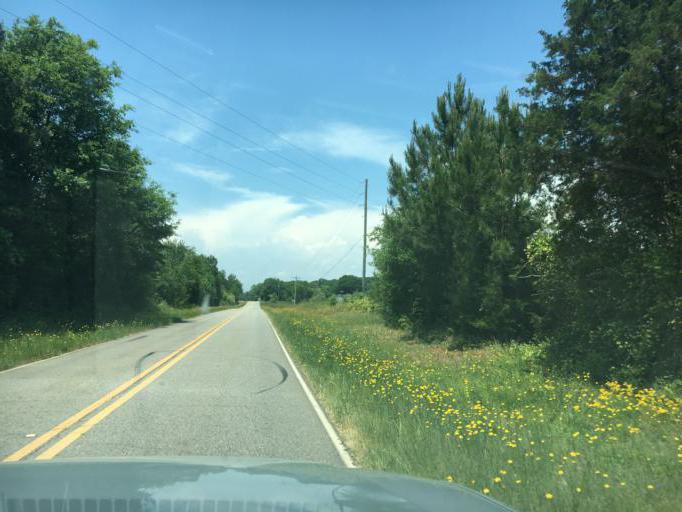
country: US
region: Georgia
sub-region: Hart County
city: Royston
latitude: 34.2974
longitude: -83.0880
